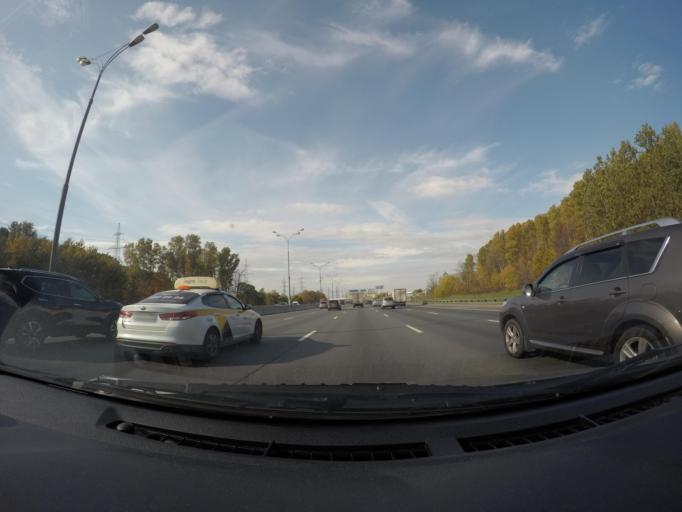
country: RU
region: Moscow
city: Lianozovo
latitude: 55.9062
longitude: 37.6022
